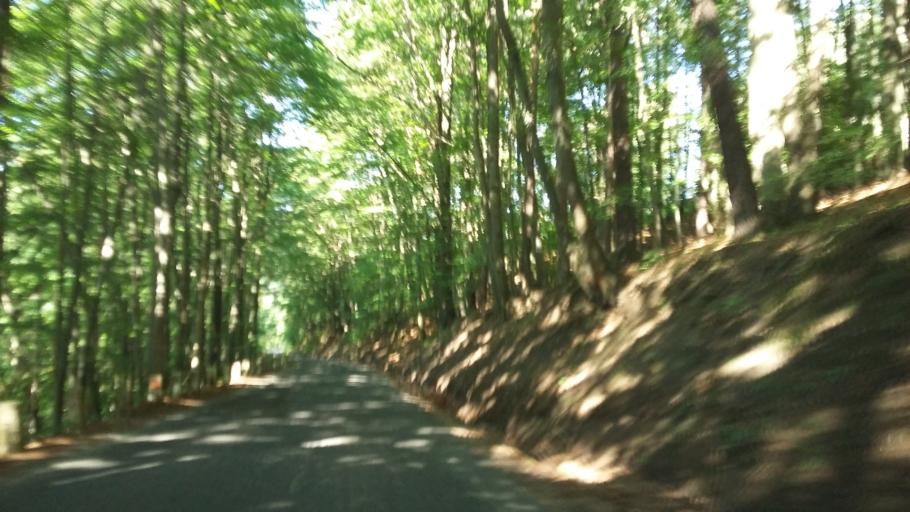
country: CZ
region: Liberecky
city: Mala Skala
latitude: 50.6061
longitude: 15.1900
